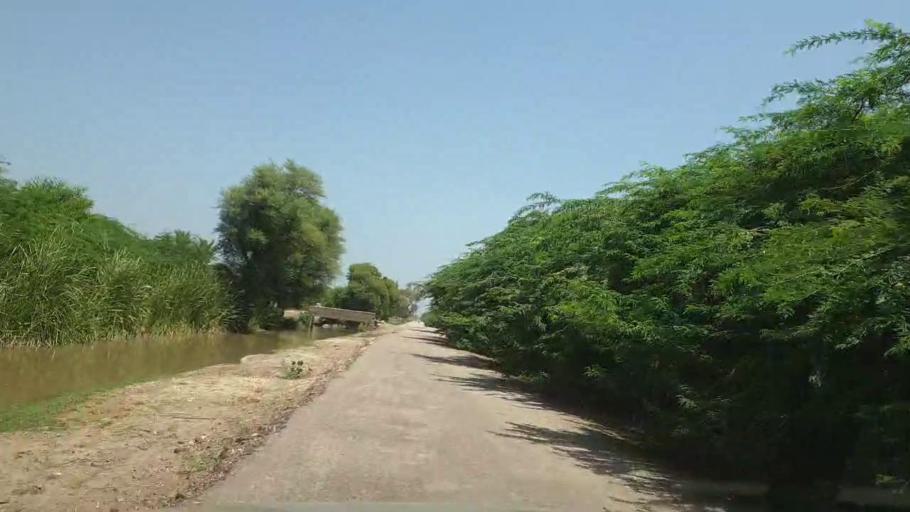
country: PK
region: Sindh
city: Rohri
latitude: 27.6283
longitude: 69.0984
